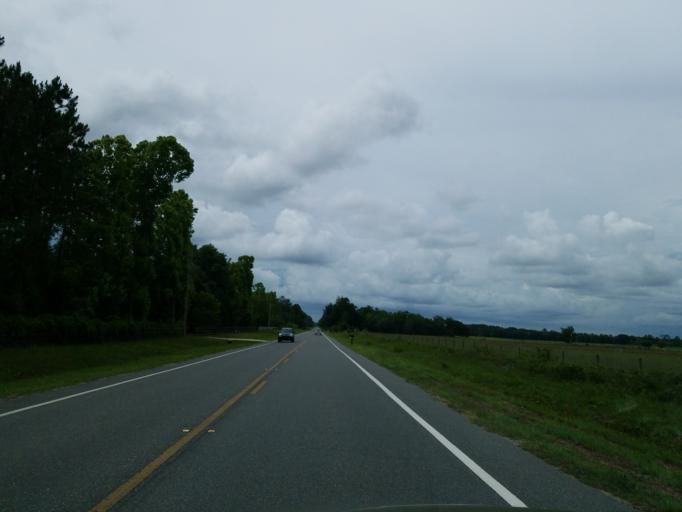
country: US
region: Florida
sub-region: Alachua County
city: High Springs
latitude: 29.8884
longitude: -82.4928
